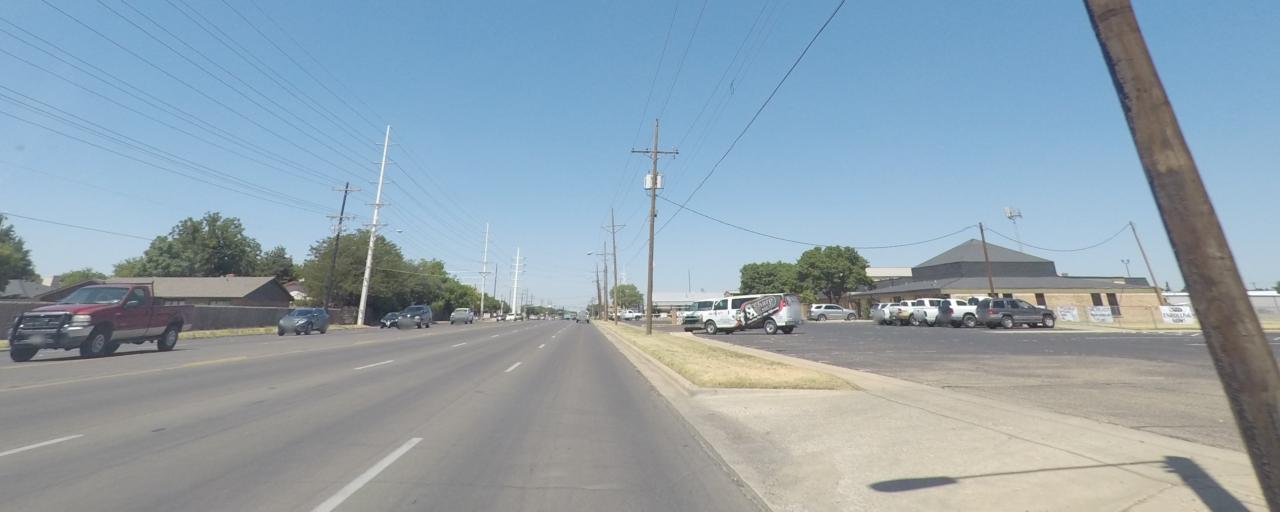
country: US
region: Texas
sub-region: Lubbock County
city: Lubbock
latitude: 33.5165
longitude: -101.8876
